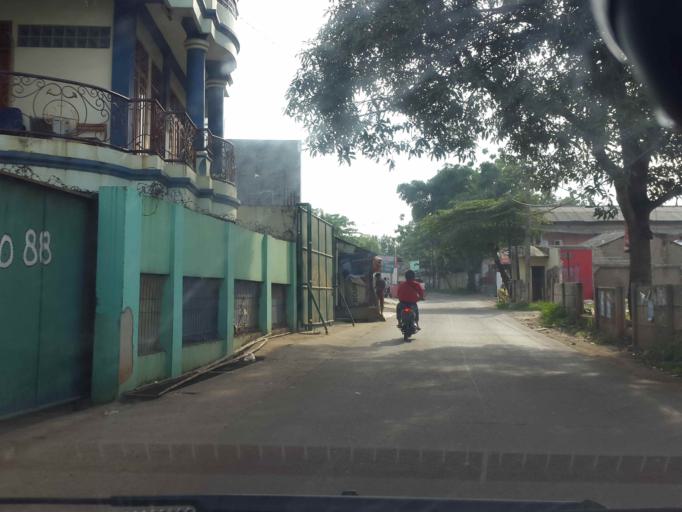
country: ID
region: West Java
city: Ciputat
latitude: -6.2626
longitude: 106.6744
